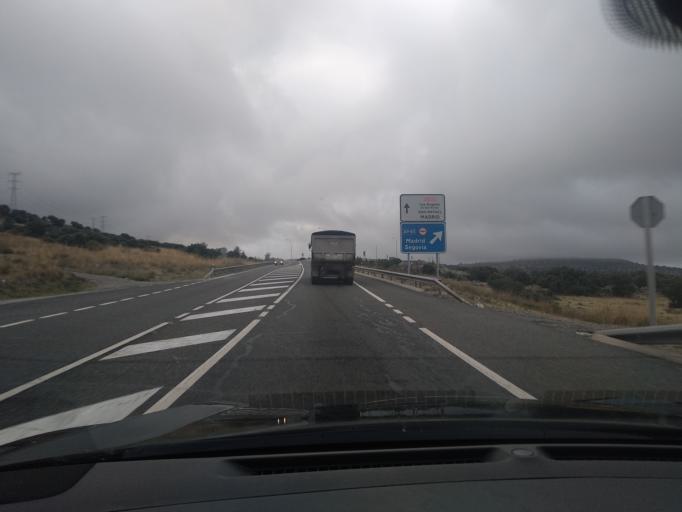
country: ES
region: Castille and Leon
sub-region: Provincia de Segovia
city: Otero de Herreros
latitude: 40.7928
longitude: -4.2160
